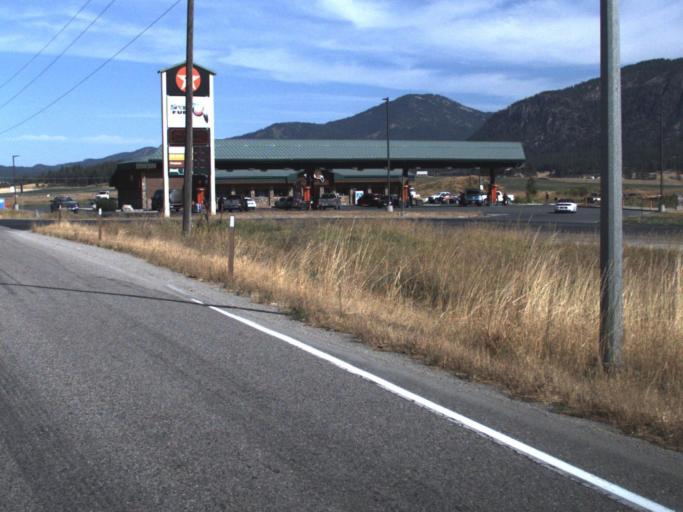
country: US
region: Washington
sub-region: Stevens County
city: Chewelah
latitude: 48.2402
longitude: -117.7152
